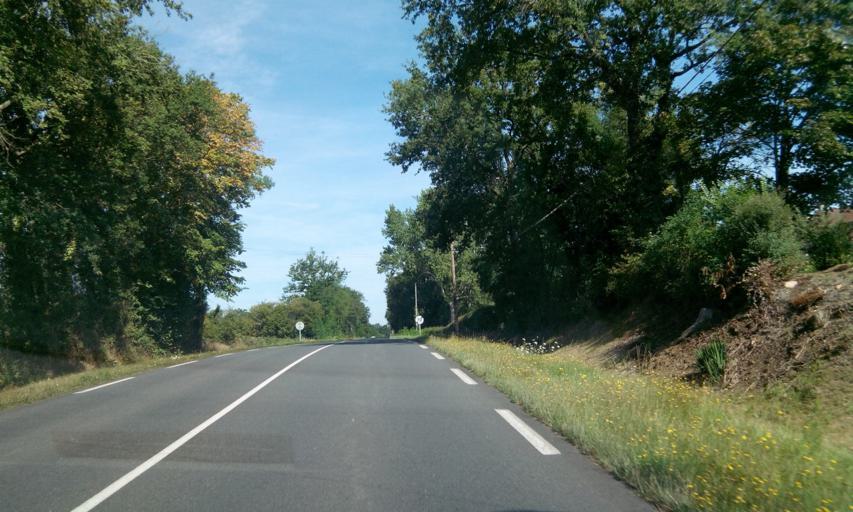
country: FR
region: Poitou-Charentes
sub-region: Departement de la Charente
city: Etagnac
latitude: 45.9358
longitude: 0.7358
